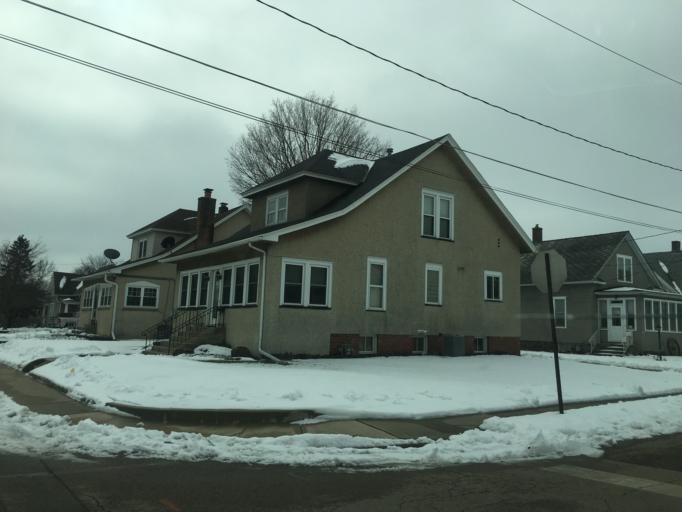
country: US
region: Illinois
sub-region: LaSalle County
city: Peru
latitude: 41.3322
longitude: -89.1253
